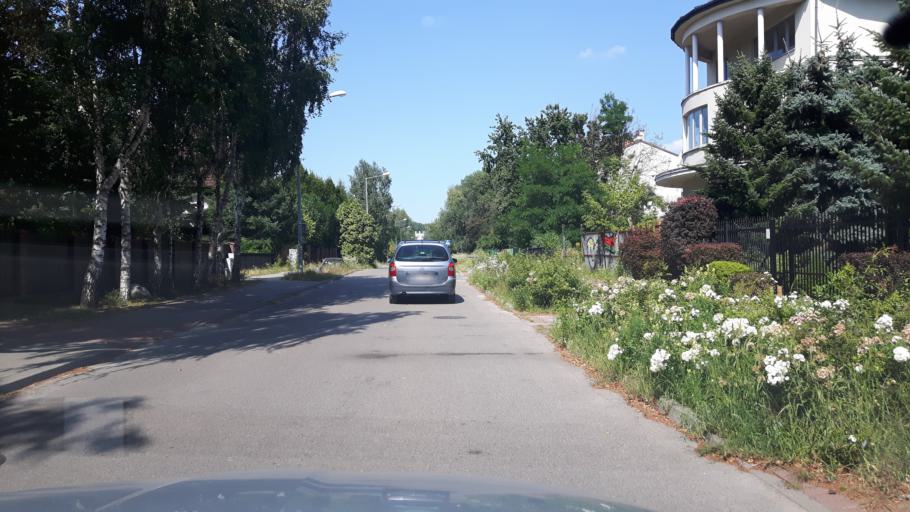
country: PL
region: Masovian Voivodeship
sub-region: Warszawa
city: Wesola
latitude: 52.2194
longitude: 21.2278
